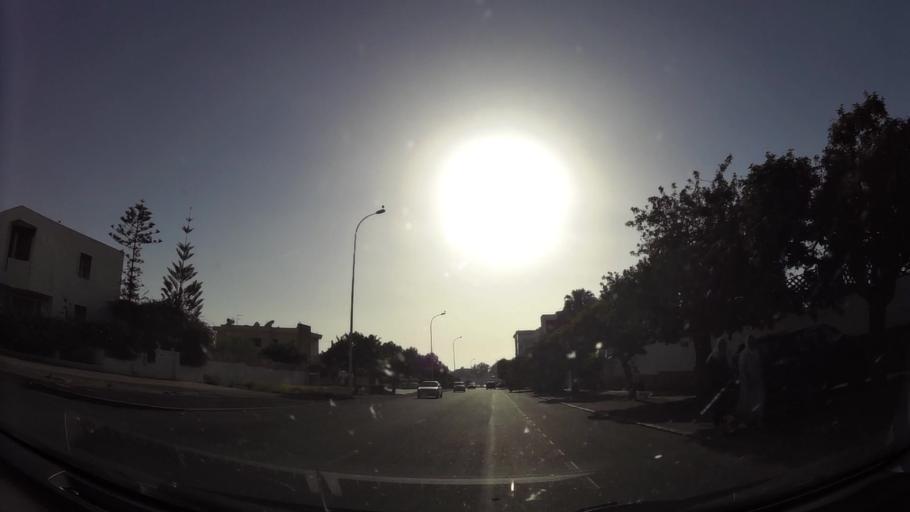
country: MA
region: Souss-Massa-Draa
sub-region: Agadir-Ida-ou-Tnan
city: Agadir
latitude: 30.4256
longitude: -9.5881
